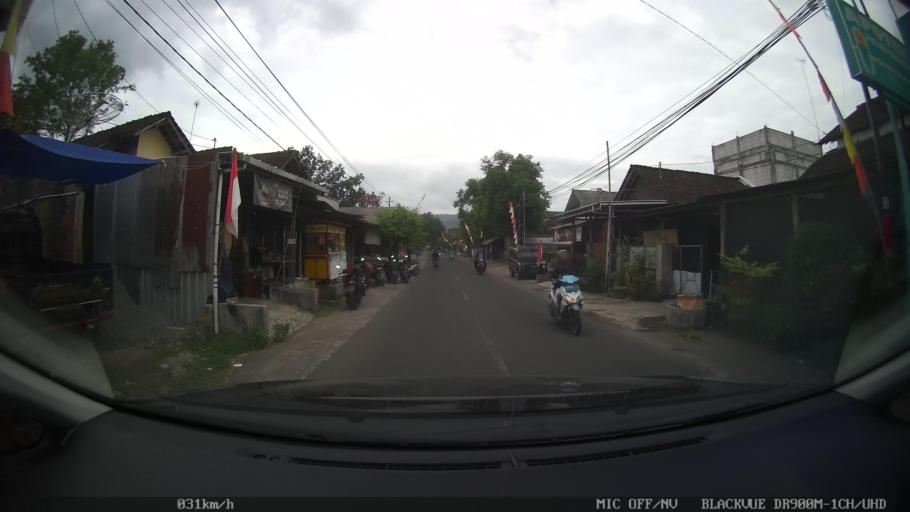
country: ID
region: Daerah Istimewa Yogyakarta
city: Sewon
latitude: -7.8781
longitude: 110.4117
